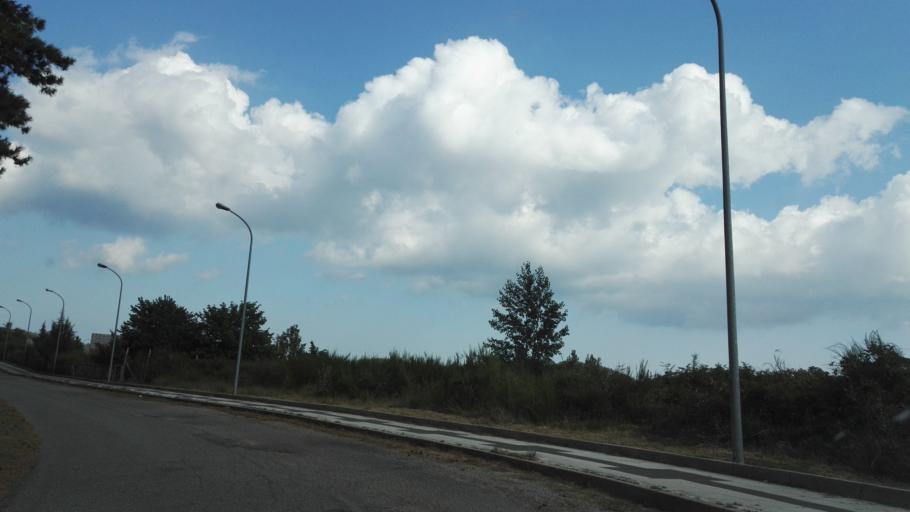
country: IT
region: Calabria
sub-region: Provincia di Vibo-Valentia
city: Nardodipace
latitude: 38.4771
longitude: 16.3414
